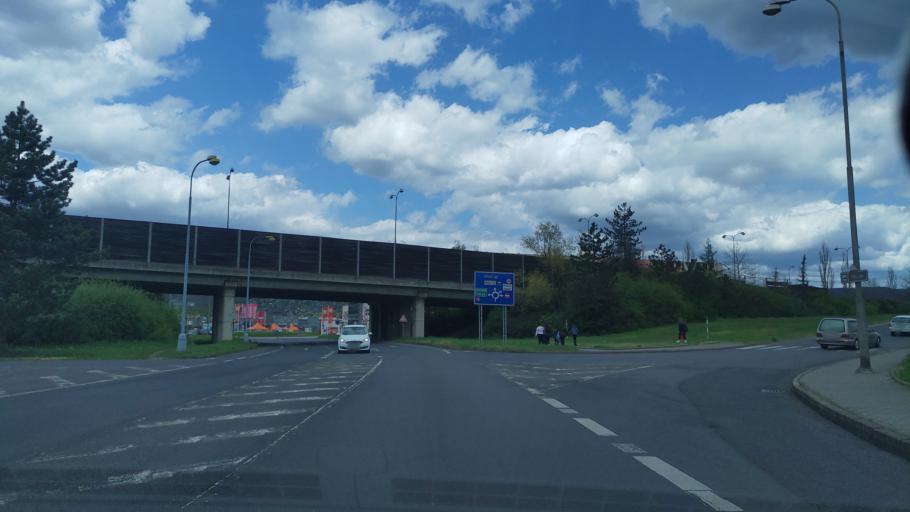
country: CZ
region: Ustecky
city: Trmice
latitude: 50.6473
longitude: 14.0057
